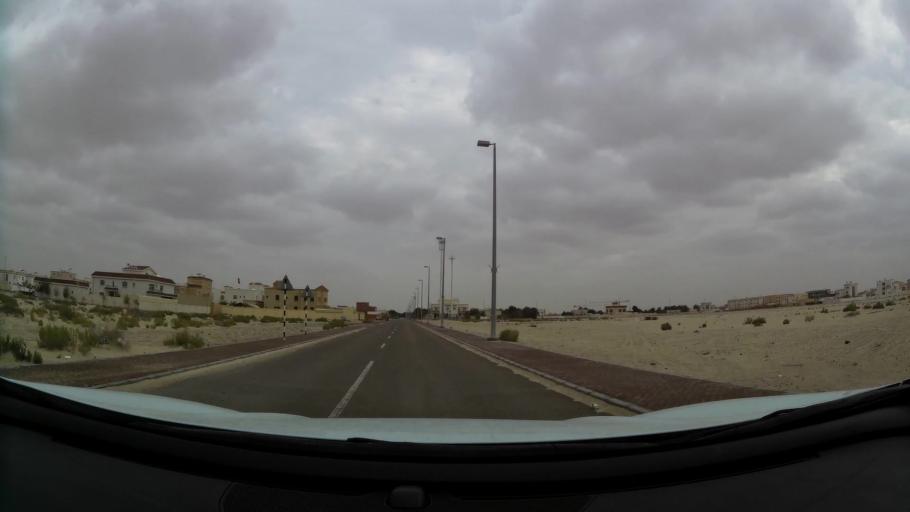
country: AE
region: Abu Dhabi
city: Abu Dhabi
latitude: 24.3797
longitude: 54.6348
